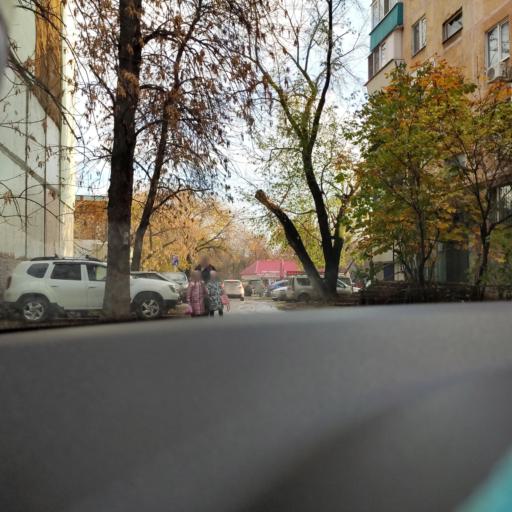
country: RU
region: Samara
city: Samara
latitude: 53.2538
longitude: 50.2349
